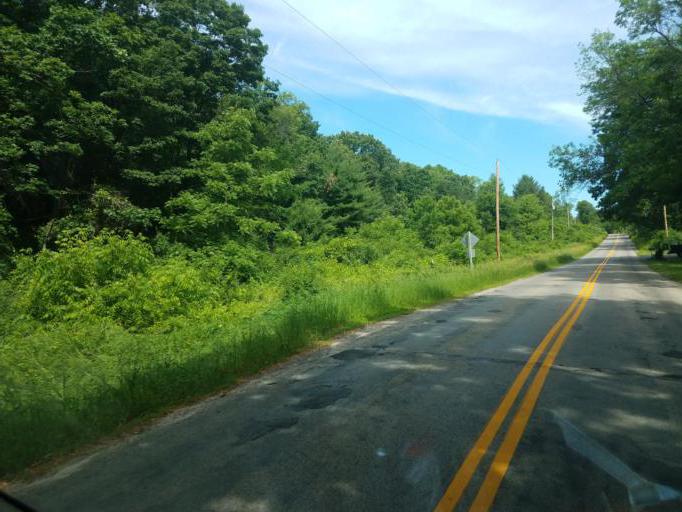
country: US
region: Wisconsin
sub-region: Columbia County
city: Wisconsin Dells
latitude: 43.6413
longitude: -89.7698
